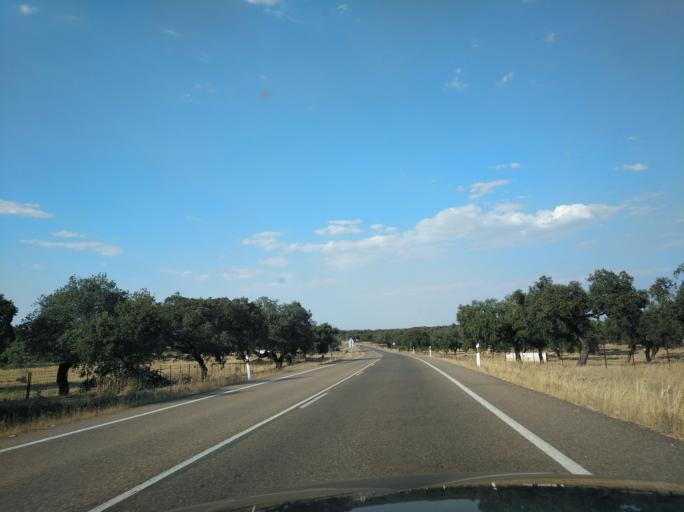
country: ES
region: Extremadura
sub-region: Provincia de Badajoz
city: Villanueva del Fresno
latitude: 38.4019
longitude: -7.1423
